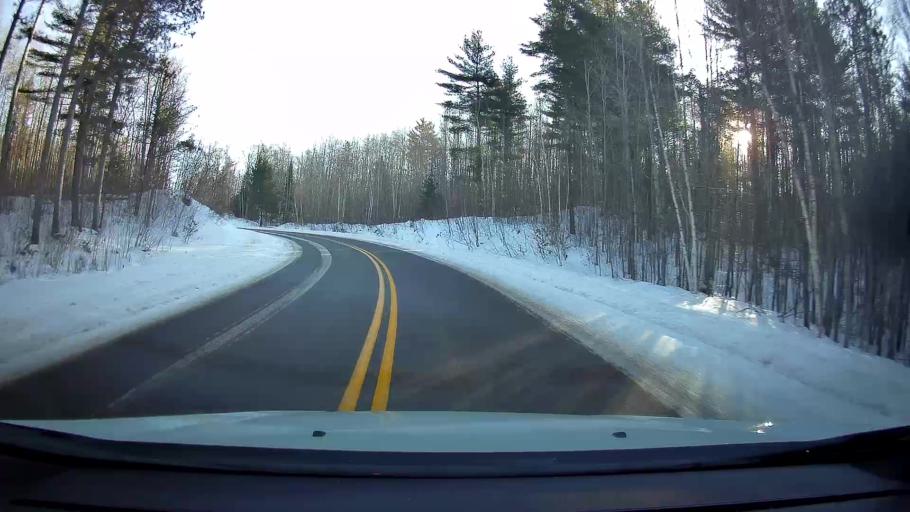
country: US
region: Wisconsin
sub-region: Sawyer County
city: Little Round Lake
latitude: 46.1092
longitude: -91.3020
